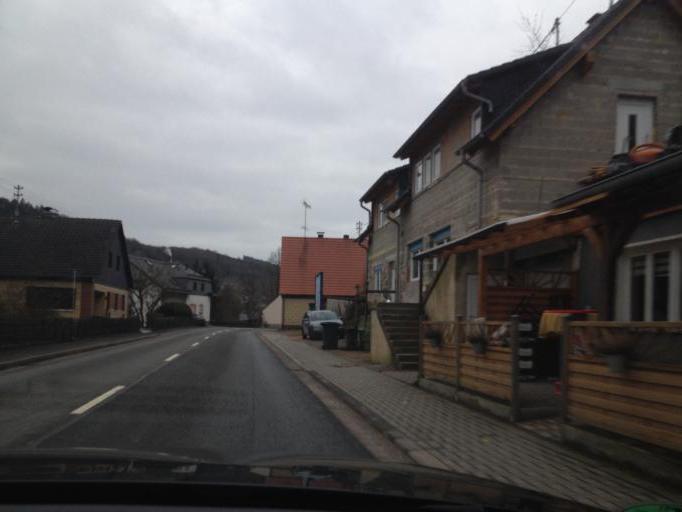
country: DE
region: Saarland
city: Nohfelden
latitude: 49.5895
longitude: 7.1413
